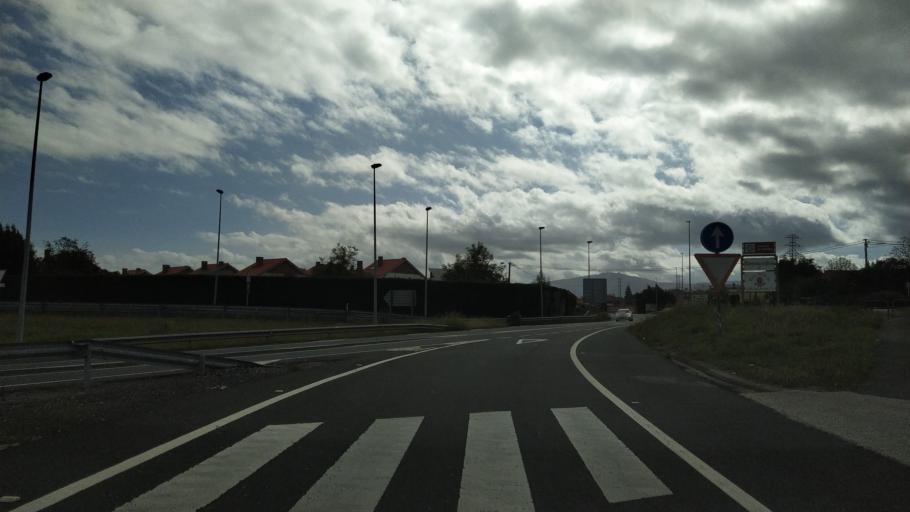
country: ES
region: Cantabria
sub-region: Provincia de Cantabria
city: Camargo
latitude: 43.4367
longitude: -3.8615
